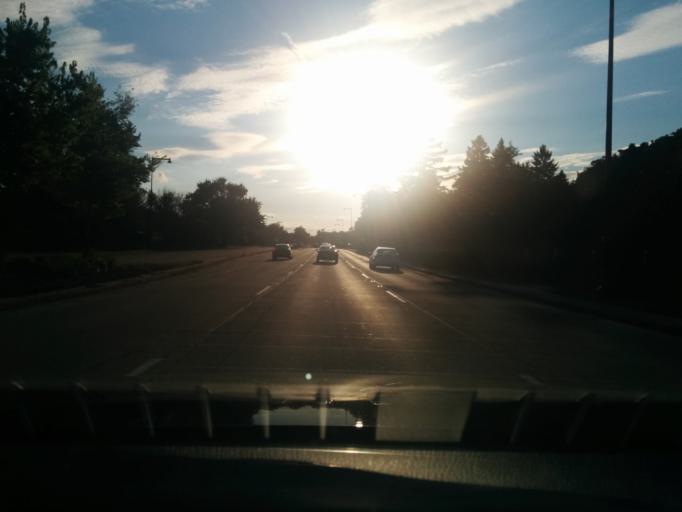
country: US
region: Illinois
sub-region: DuPage County
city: Bloomingdale
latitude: 41.9572
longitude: -88.0674
